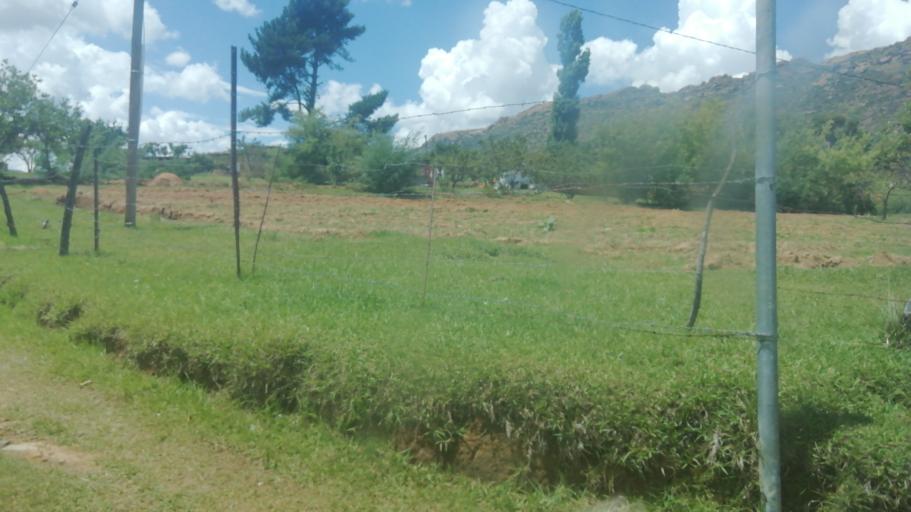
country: LS
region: Maseru
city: Nako
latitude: -29.6207
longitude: 27.5173
